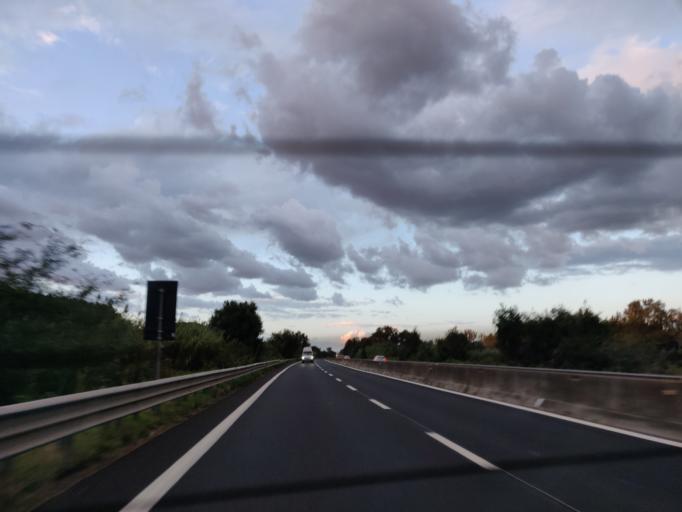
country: IT
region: Tuscany
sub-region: Provincia di Livorno
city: Donoratico
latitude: 43.1392
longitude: 10.5510
